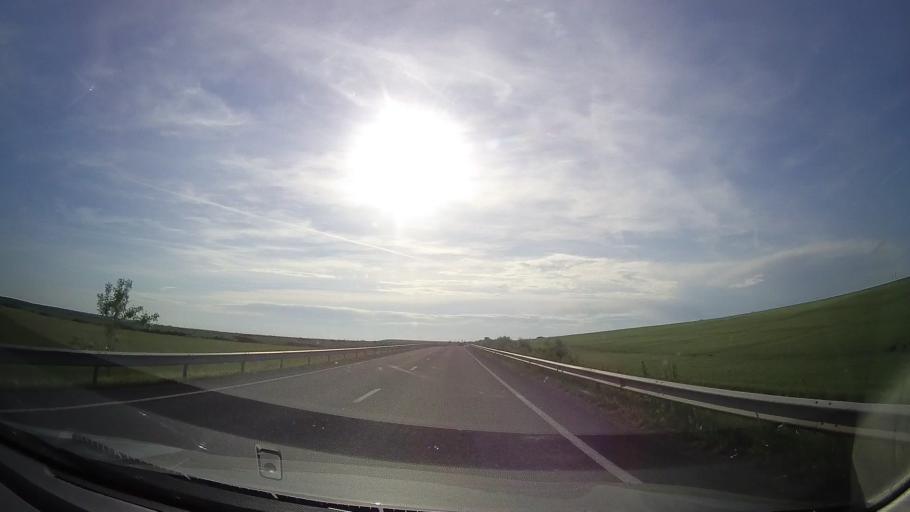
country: RO
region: Timis
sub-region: Comuna Topolovatu Mare
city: Topolovatu Mare
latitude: 45.7916
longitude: 21.5684
